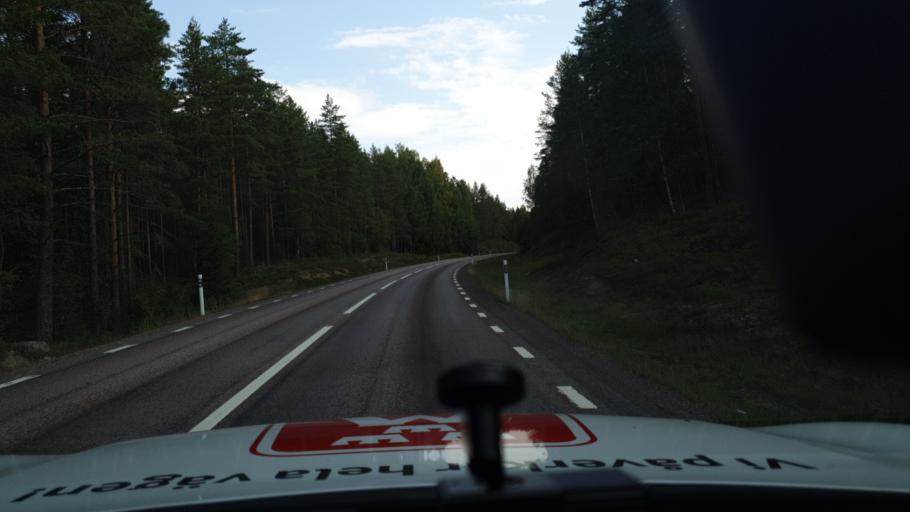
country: SE
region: Vaermland
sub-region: Hagfors Kommun
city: Ekshaerad
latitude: 60.4786
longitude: 13.3087
